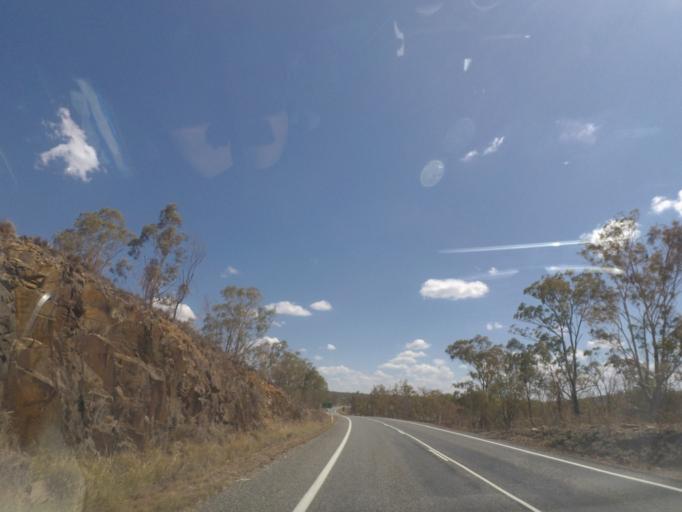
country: AU
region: Queensland
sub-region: Southern Downs
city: Warwick
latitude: -28.2104
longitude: 151.5649
